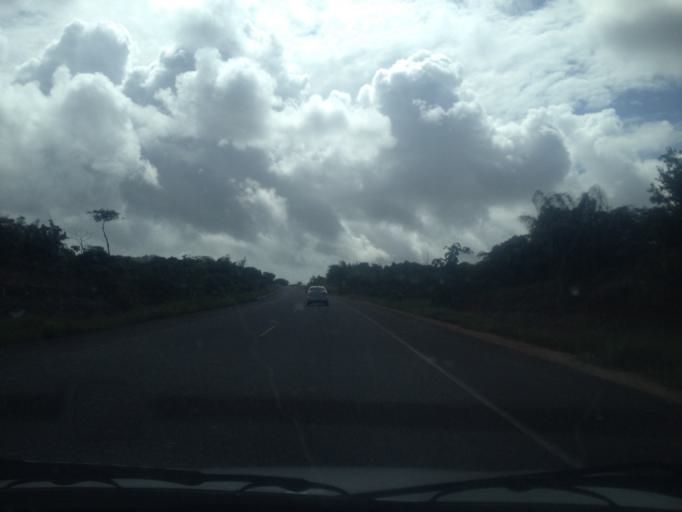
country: BR
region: Bahia
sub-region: Entre Rios
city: Entre Rios
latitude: -12.1979
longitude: -37.8234
